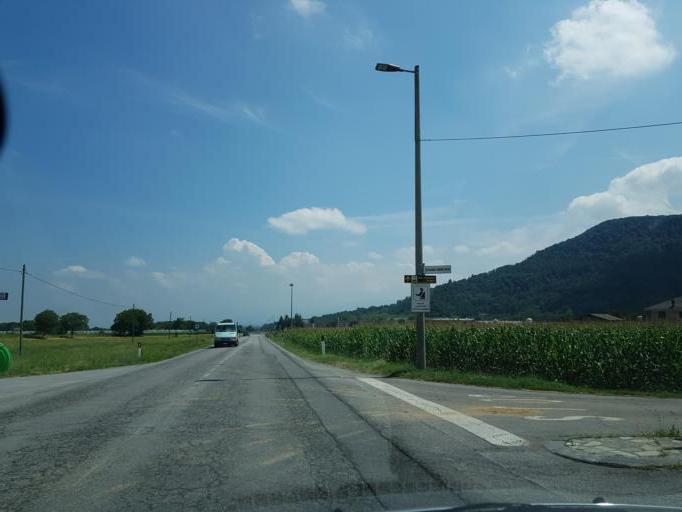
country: IT
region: Piedmont
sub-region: Provincia di Cuneo
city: Montemale di Cuneo
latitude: 44.4514
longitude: 7.3903
